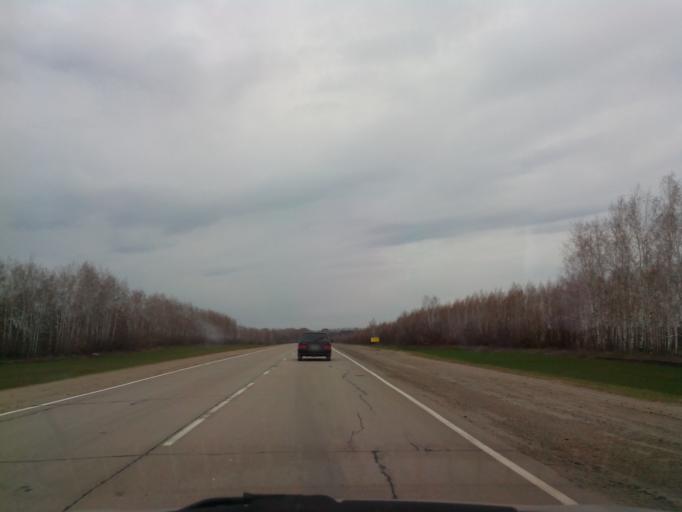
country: RU
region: Tambov
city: Znamenka
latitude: 52.3838
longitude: 41.4101
